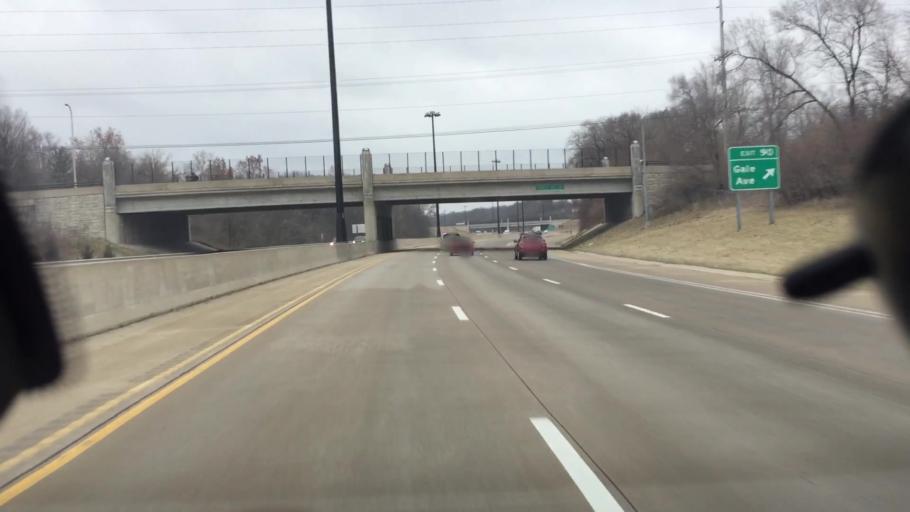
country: US
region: Illinois
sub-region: Peoria County
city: West Peoria
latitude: 40.7257
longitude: -89.6206
